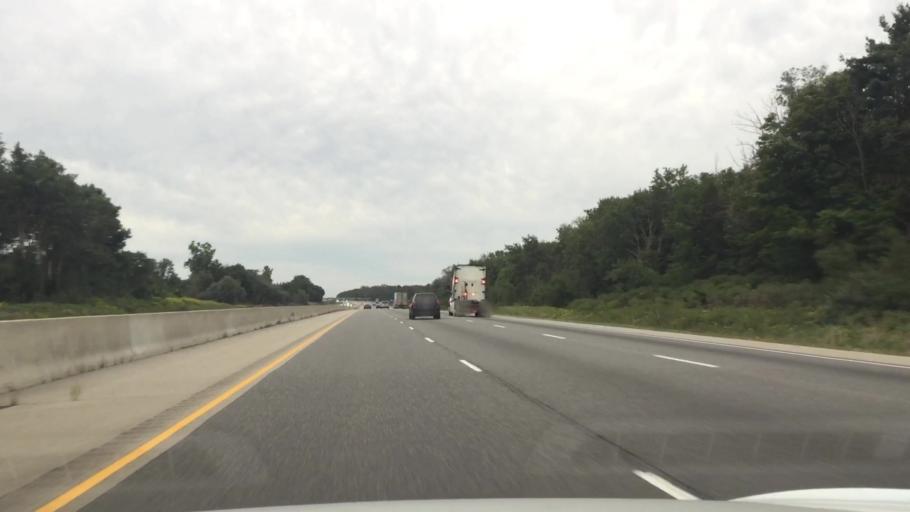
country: CA
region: Ontario
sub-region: Oxford County
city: Woodstock
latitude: 43.1761
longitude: -80.6516
